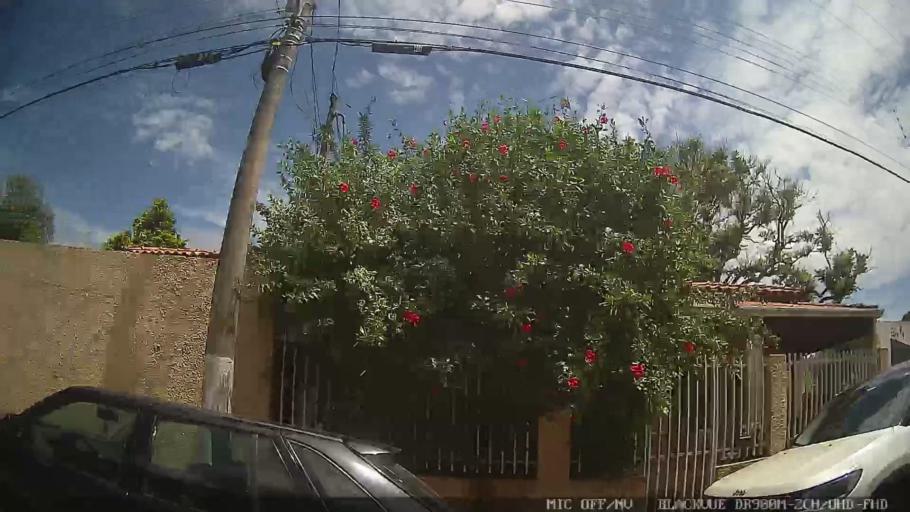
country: BR
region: Sao Paulo
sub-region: Laranjal Paulista
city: Laranjal Paulista
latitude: -23.0527
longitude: -47.8391
